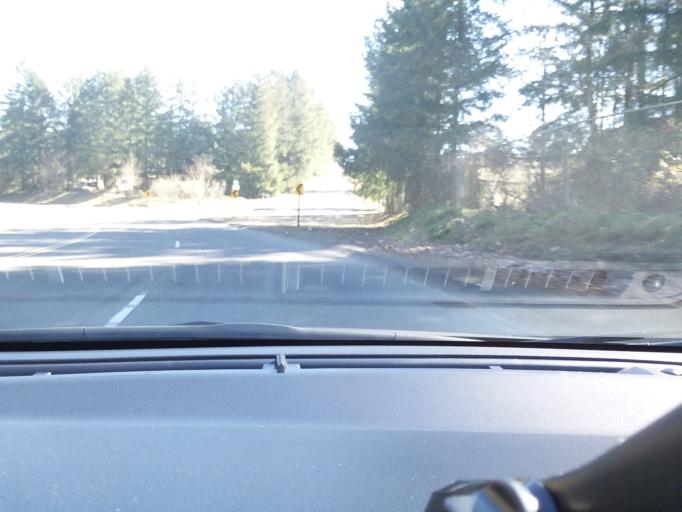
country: US
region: Washington
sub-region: Pierce County
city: Waller
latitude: 47.1917
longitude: -122.3501
